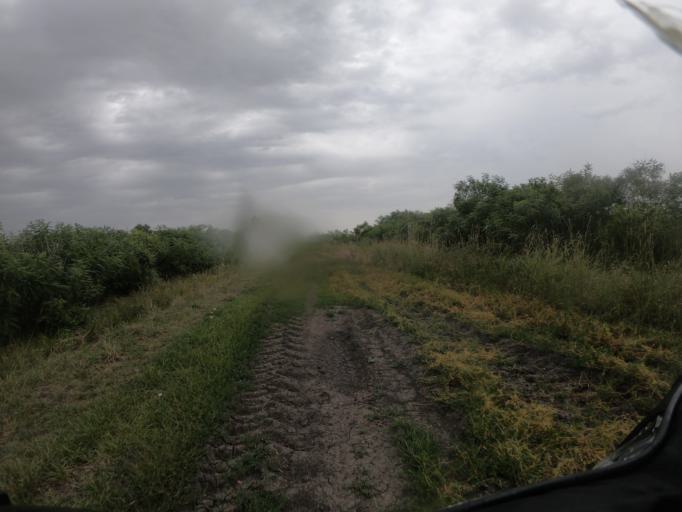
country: HU
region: Heves
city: Poroszlo
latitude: 47.6909
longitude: 20.5777
